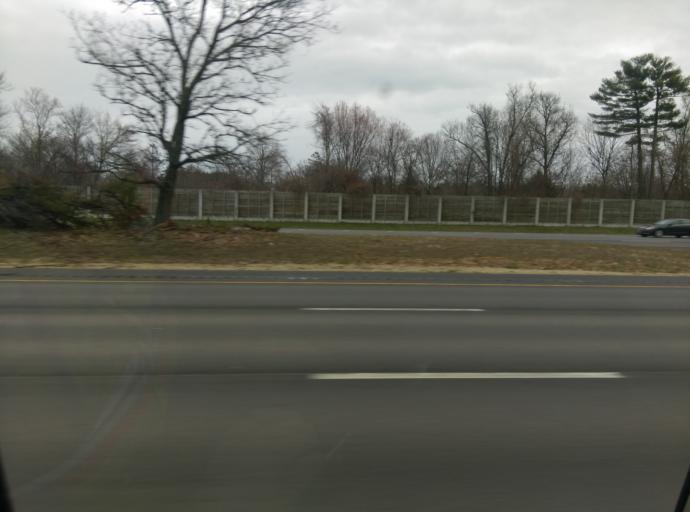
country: US
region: New Hampshire
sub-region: Rockingham County
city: Seabrook
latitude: 42.8909
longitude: -70.8811
